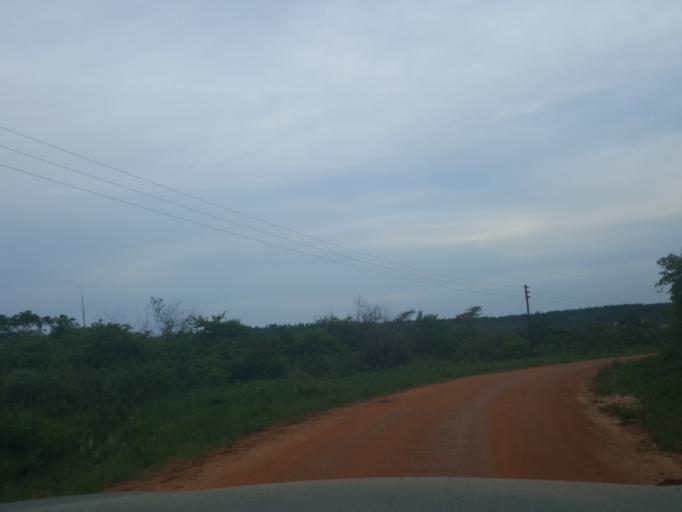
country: ZA
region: Limpopo
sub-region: Mopani District Municipality
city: Hoedspruit
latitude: -24.5964
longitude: 30.9263
